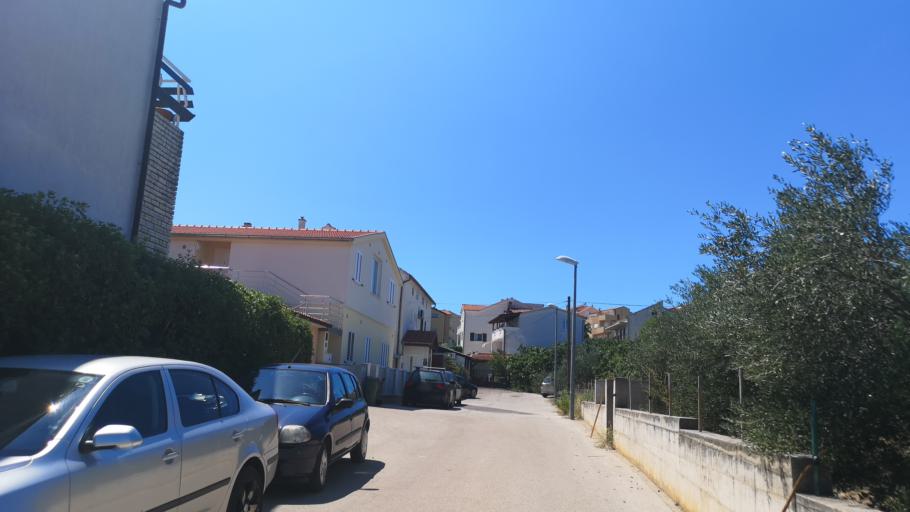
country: HR
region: Sibensko-Kniniska
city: Vodice
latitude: 43.7630
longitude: 15.7687
